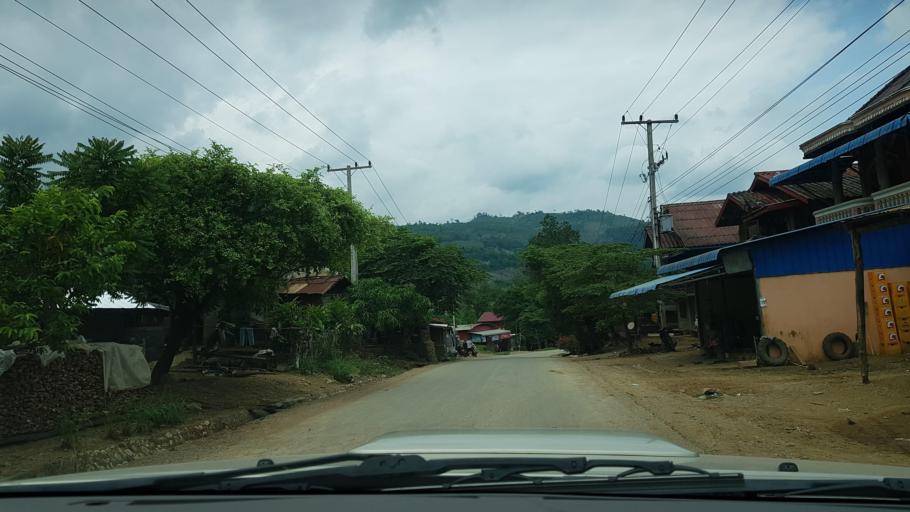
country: TH
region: Nan
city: Chaloem Phra Kiat
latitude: 19.9905
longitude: 101.2777
